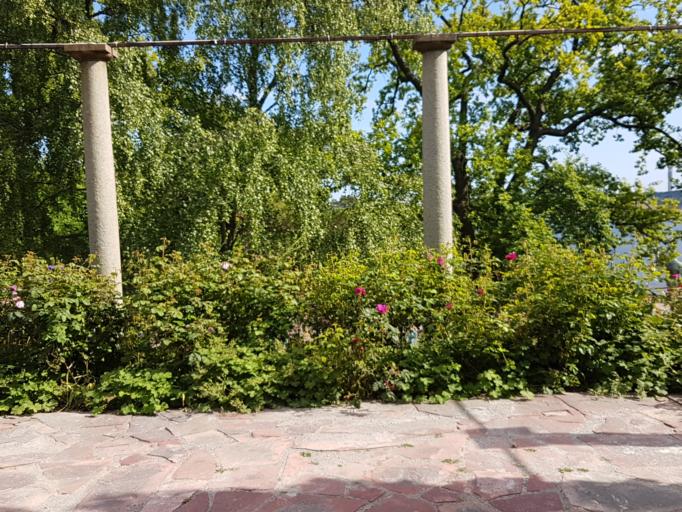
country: SE
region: Stockholm
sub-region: Lidingo
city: Lidingoe
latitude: 59.3591
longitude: 18.1212
